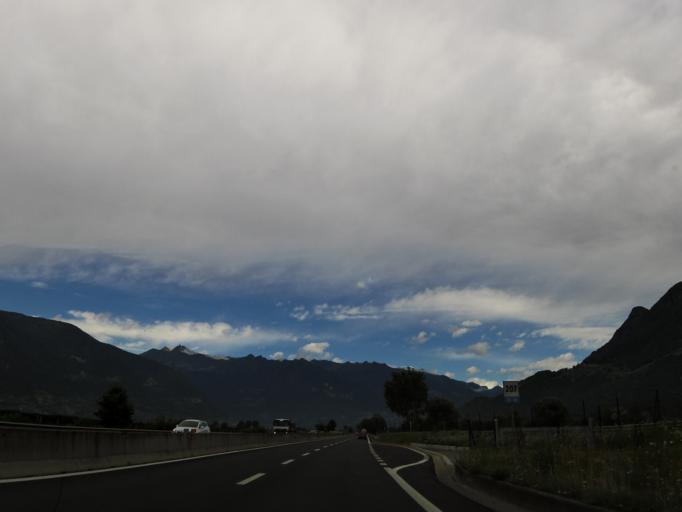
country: IT
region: Trentino-Alto Adige
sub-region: Bolzano
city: Postal
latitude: 46.5978
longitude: 11.1857
